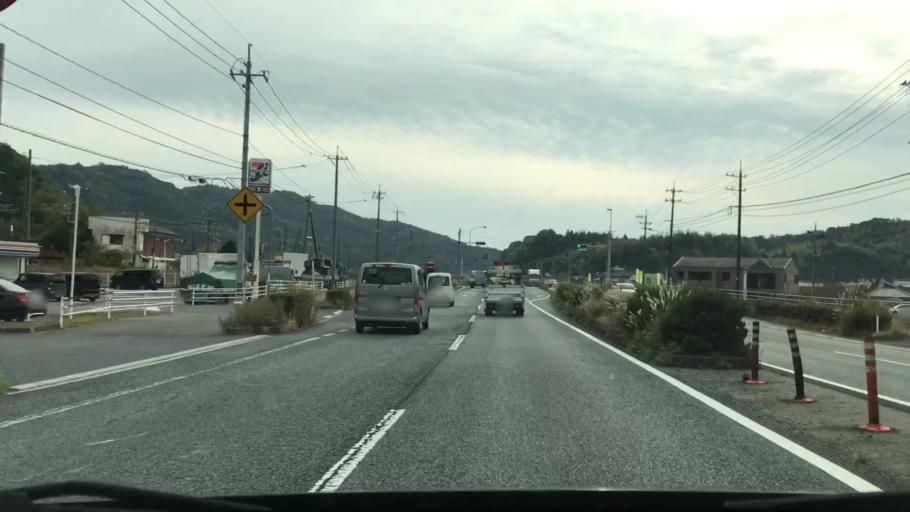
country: JP
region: Yamaguchi
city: Tokuyama
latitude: 34.0772
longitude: 131.7068
